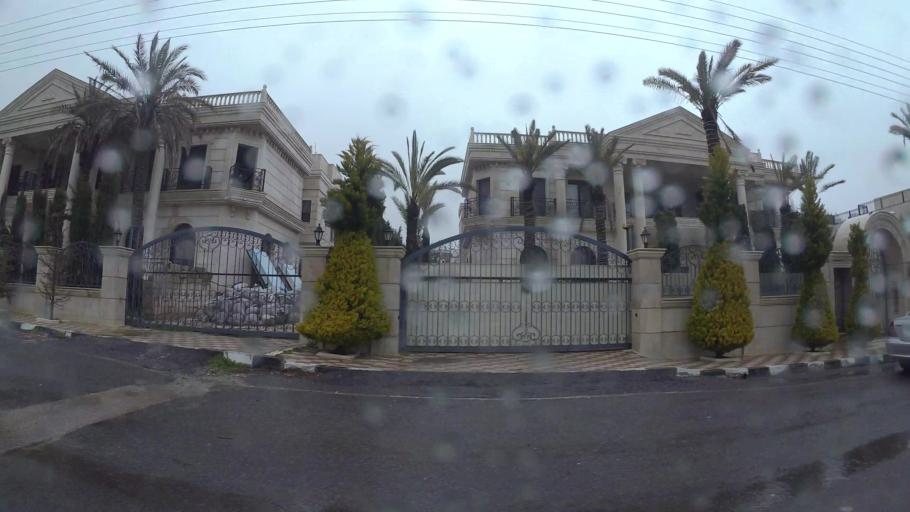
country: JO
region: Amman
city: Wadi as Sir
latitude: 31.9949
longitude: 35.8246
